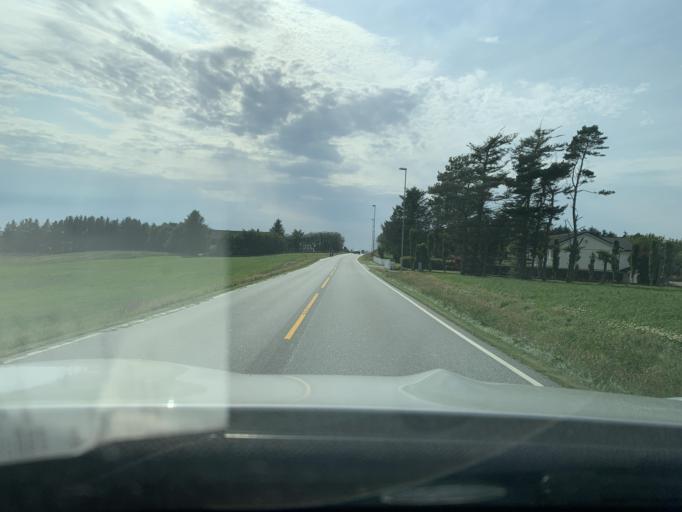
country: NO
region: Rogaland
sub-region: Time
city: Bryne
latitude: 58.7396
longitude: 5.6215
